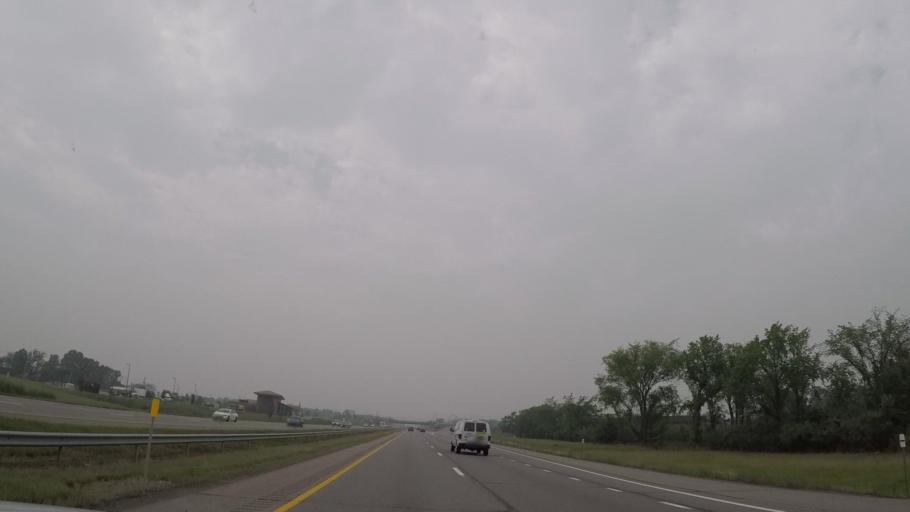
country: US
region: New York
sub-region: Erie County
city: Grandyle Village
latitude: 43.0173
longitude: -78.9715
